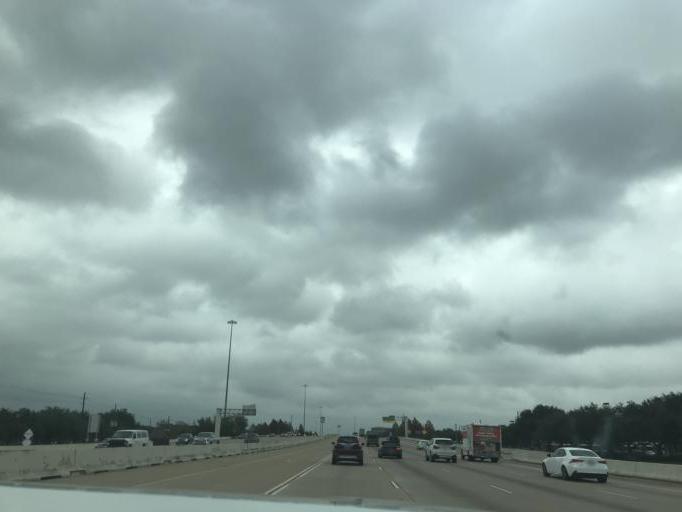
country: US
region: Texas
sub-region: Fort Bend County
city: Sugar Land
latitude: 29.6041
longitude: -95.6165
